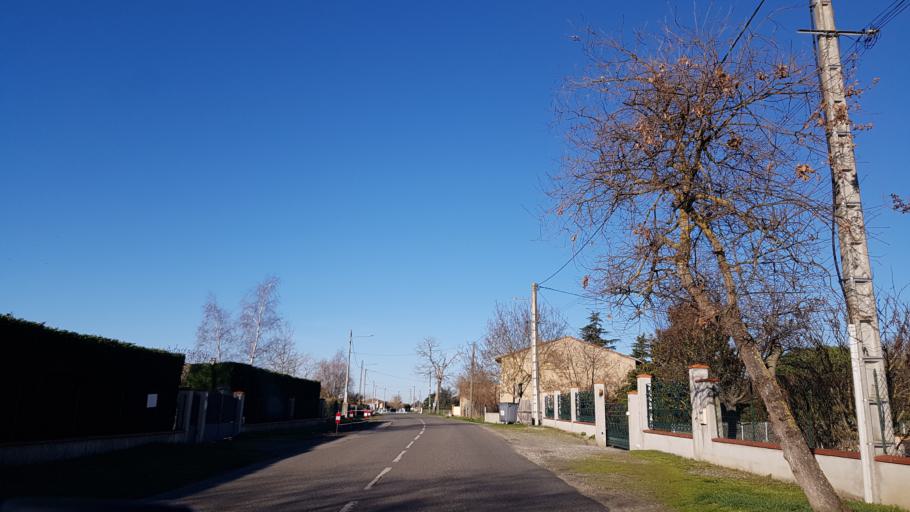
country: FR
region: Midi-Pyrenees
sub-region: Departement de la Haute-Garonne
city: Calmont
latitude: 43.2879
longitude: 1.6188
